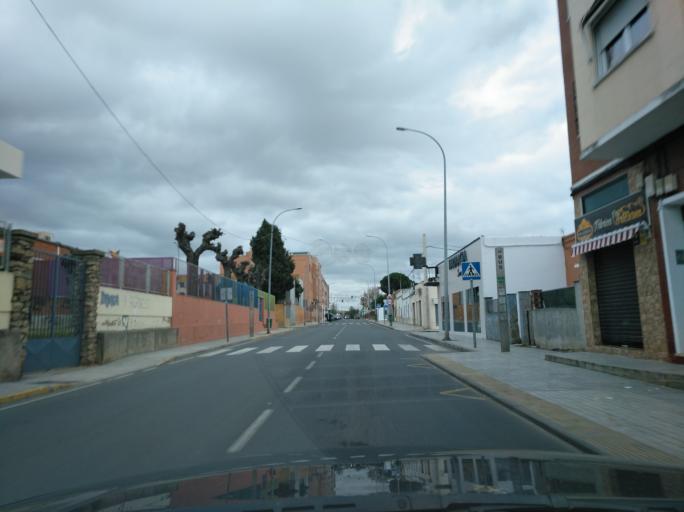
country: ES
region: Extremadura
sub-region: Provincia de Badajoz
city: Badajoz
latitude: 38.8918
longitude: -6.9792
